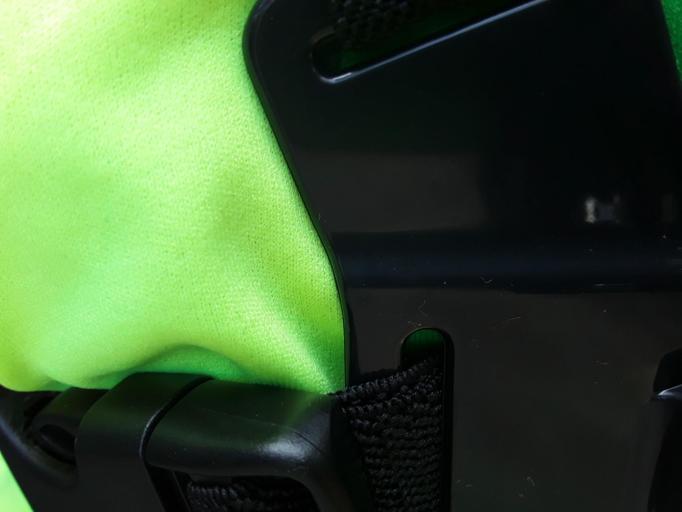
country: BR
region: Minas Gerais
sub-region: Lima Duarte
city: Lima Duarte
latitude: -21.7138
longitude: -43.9012
